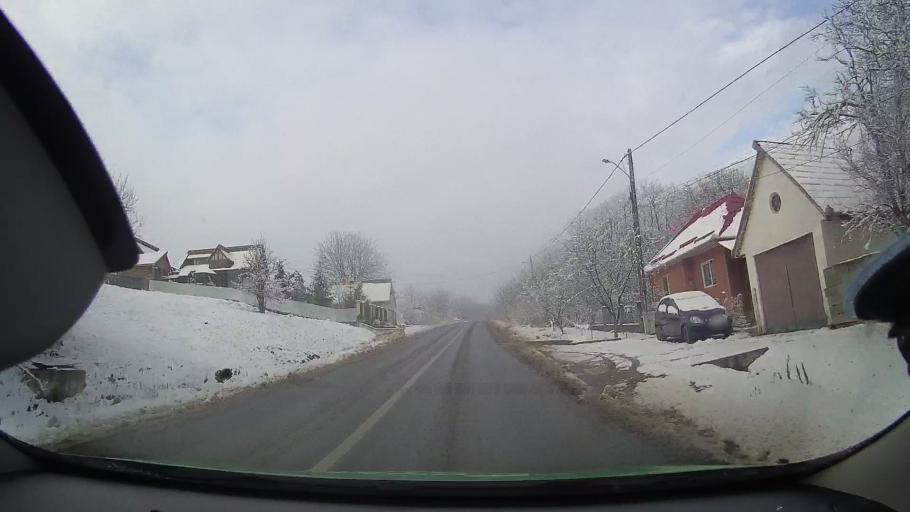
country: RO
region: Mures
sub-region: Comuna Atintis
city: Atintis
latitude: 46.4355
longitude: 24.0958
